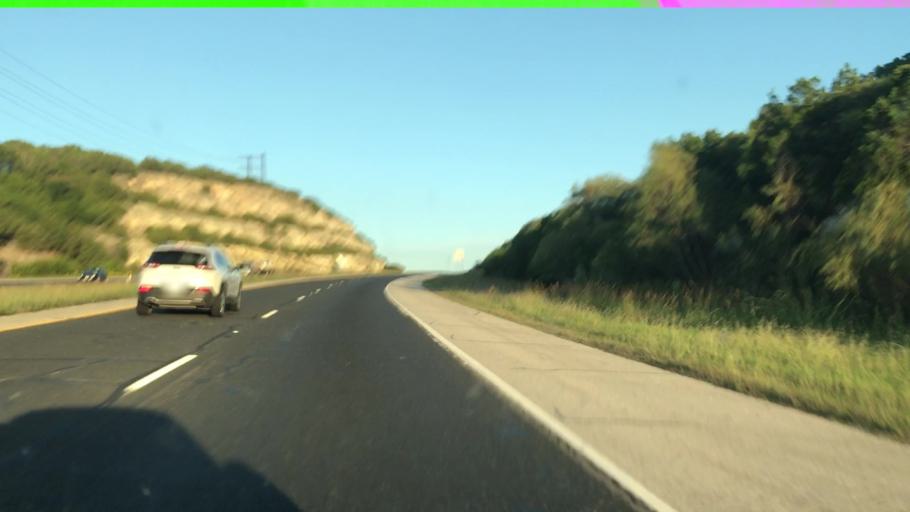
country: US
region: Texas
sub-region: Kerr County
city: Kerrville
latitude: 30.0702
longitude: -99.1022
